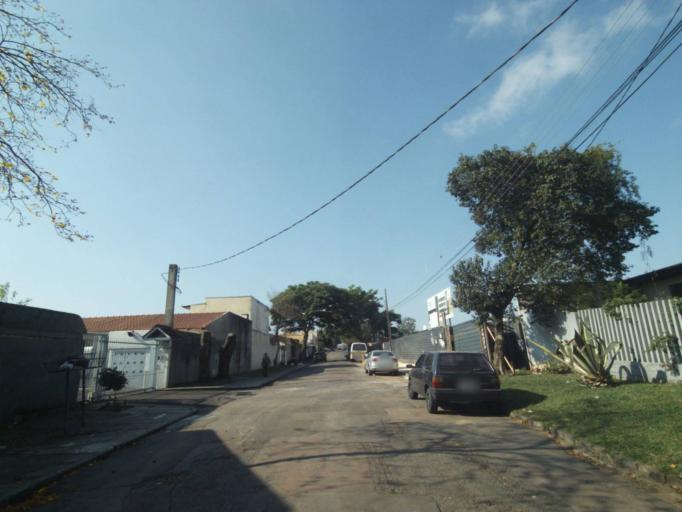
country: BR
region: Parana
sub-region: Curitiba
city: Curitiba
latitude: -25.4915
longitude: -49.3270
